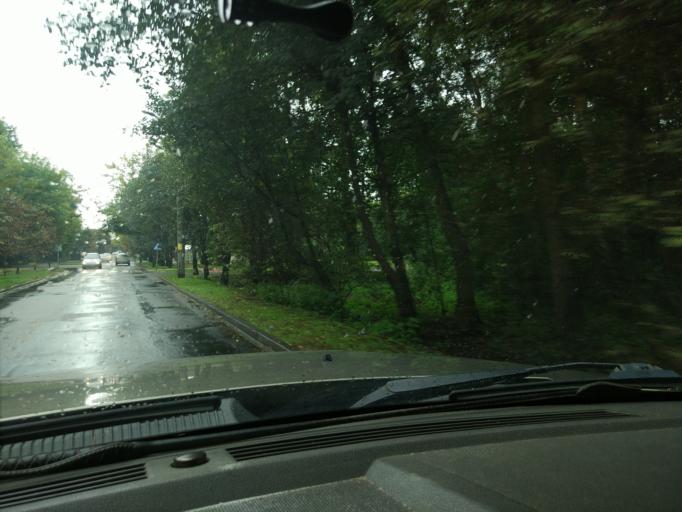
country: PL
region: Masovian Voivodeship
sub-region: Powiat grodziski
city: Podkowa Lesna
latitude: 52.1282
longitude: 20.7186
